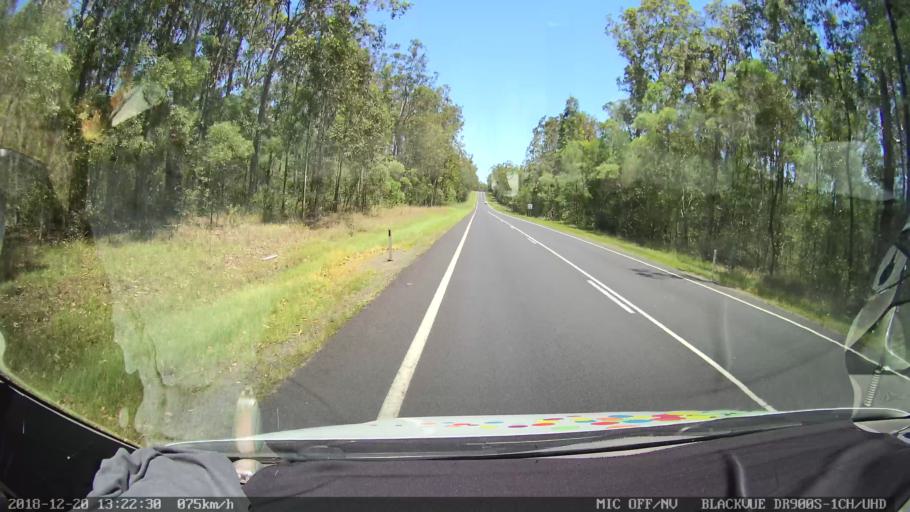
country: AU
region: New South Wales
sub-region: Richmond Valley
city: Casino
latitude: -29.0925
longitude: 153.0014
